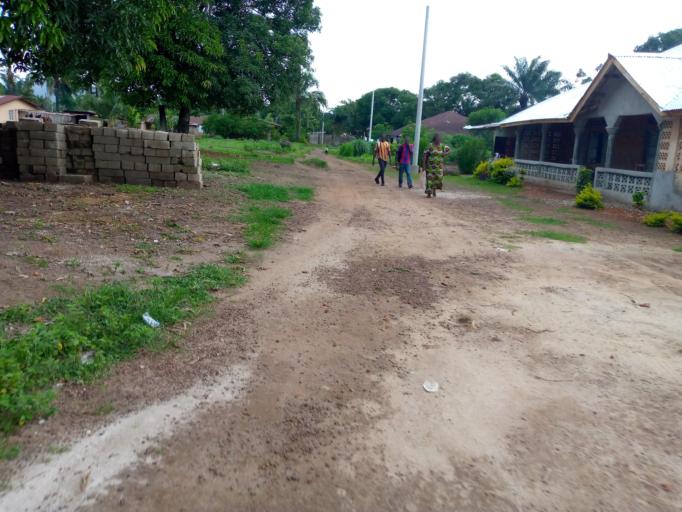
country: SL
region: Southern Province
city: Moyamba
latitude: 8.1508
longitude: -12.4345
